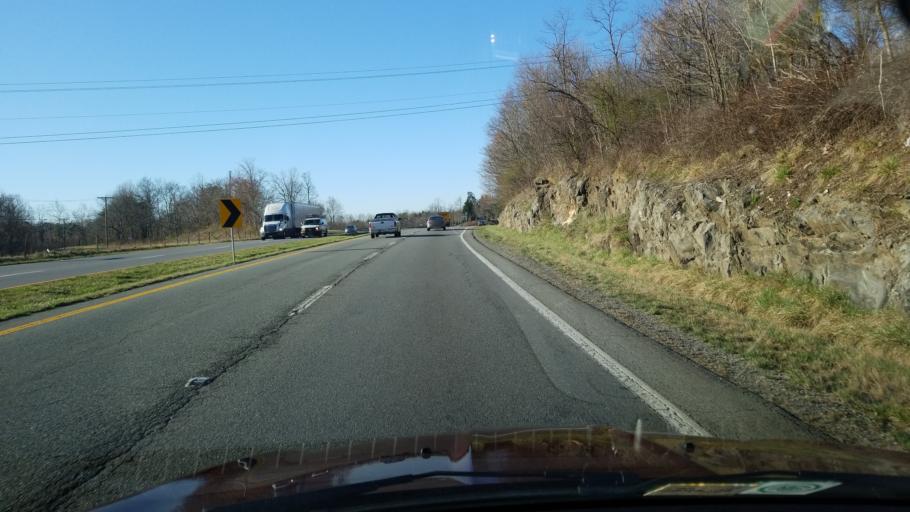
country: US
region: Virginia
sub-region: Franklin County
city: Rocky Mount
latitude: 37.0260
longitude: -79.8806
